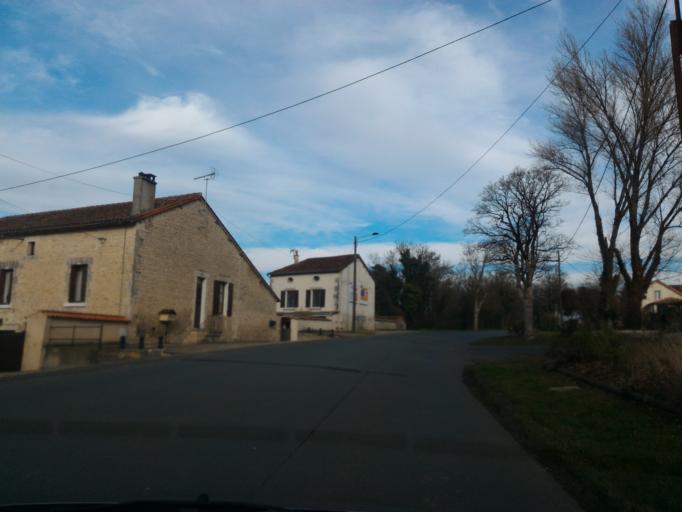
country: FR
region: Poitou-Charentes
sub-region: Departement de la Charente
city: Ruffec
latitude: 46.0338
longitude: 0.1962
